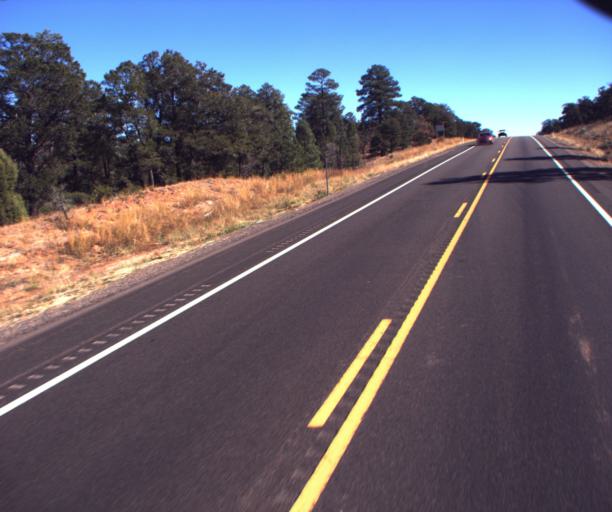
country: US
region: Arizona
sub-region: Apache County
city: Saint Michaels
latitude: 35.7066
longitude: -109.3130
